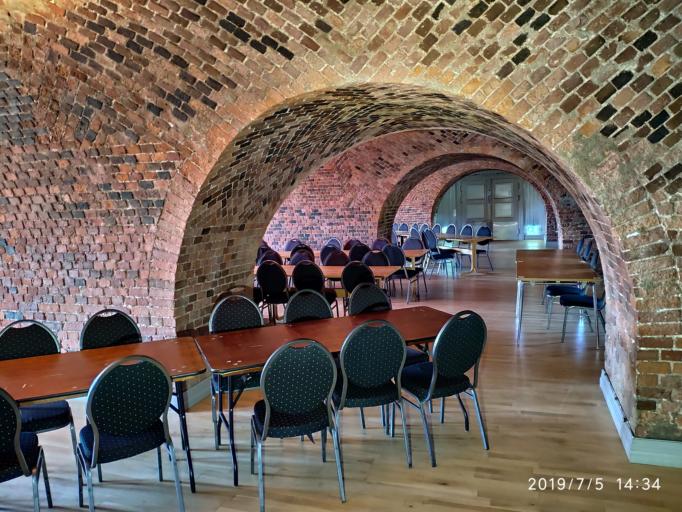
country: NO
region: Akershus
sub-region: Frogn
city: Drobak
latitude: 59.6732
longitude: 10.6070
